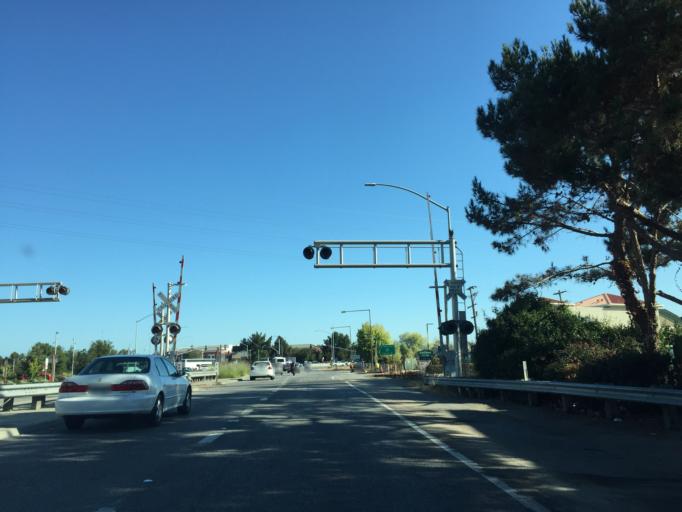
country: US
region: California
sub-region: San Mateo County
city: East Palo Alto
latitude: 37.4802
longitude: -122.1506
